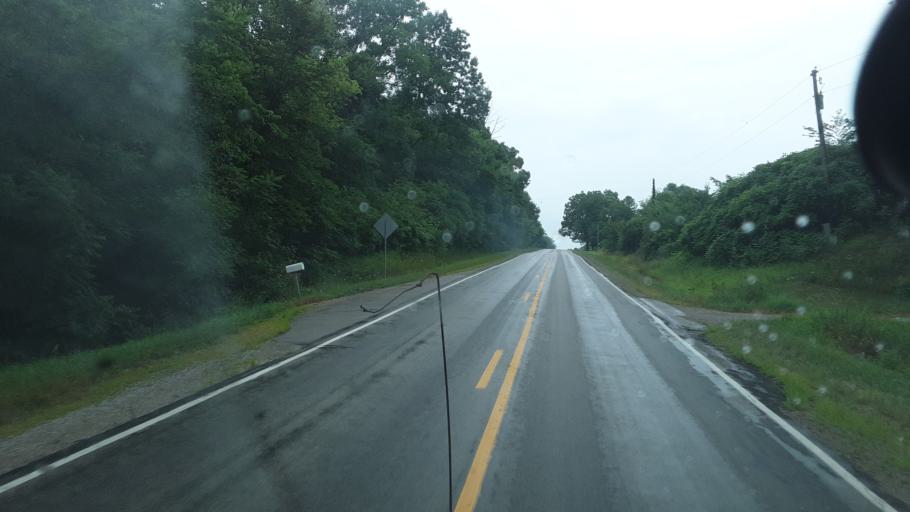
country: US
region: Indiana
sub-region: Steuben County
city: Hamilton
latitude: 41.5588
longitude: -84.8377
